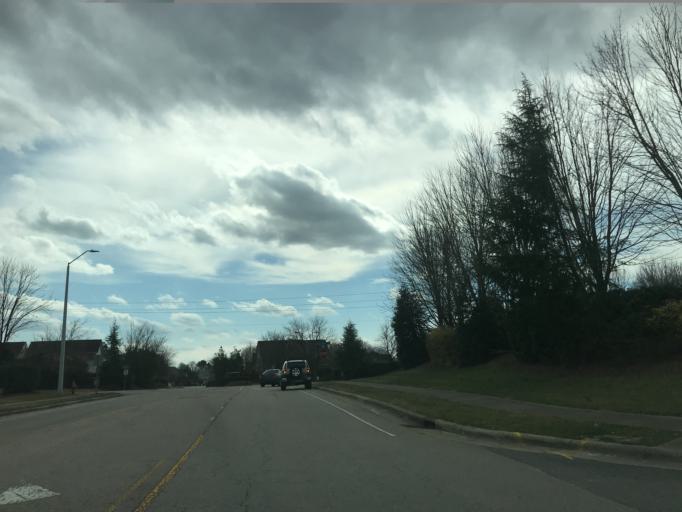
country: US
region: North Carolina
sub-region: Wake County
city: Green Level
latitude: 35.7850
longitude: -78.8562
